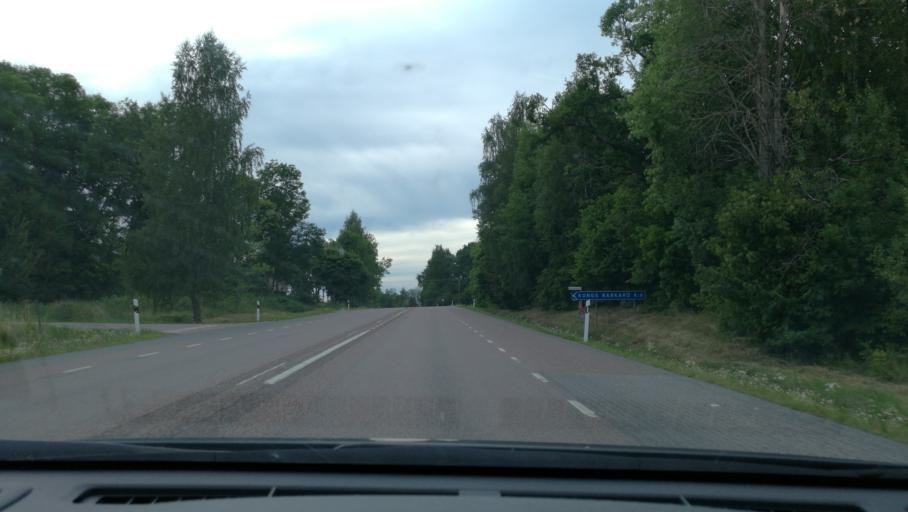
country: SE
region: Vaestmanland
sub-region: Kungsors Kommun
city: Kungsoer
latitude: 59.4495
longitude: 16.0383
